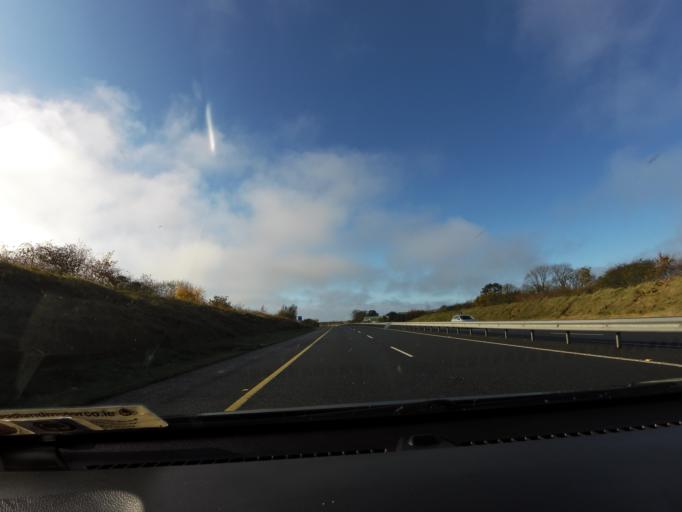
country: IE
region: Connaught
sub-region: County Galway
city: Ballinasloe
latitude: 53.3445
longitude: -8.0868
